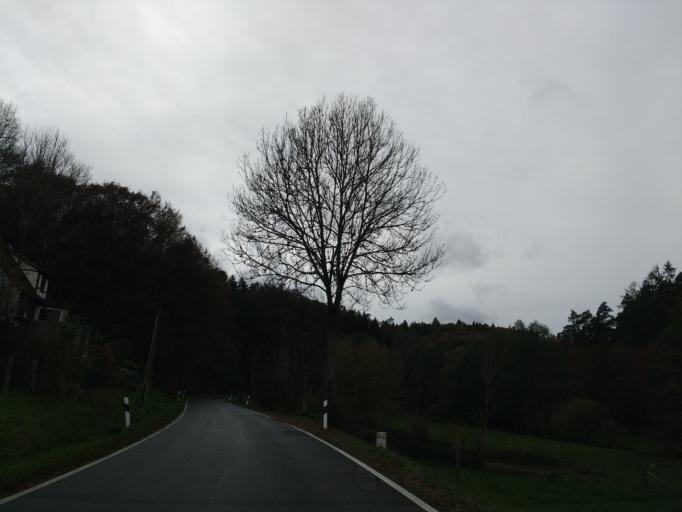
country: DE
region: Hesse
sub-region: Regierungsbezirk Kassel
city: Vohl
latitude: 51.1974
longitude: 8.9438
